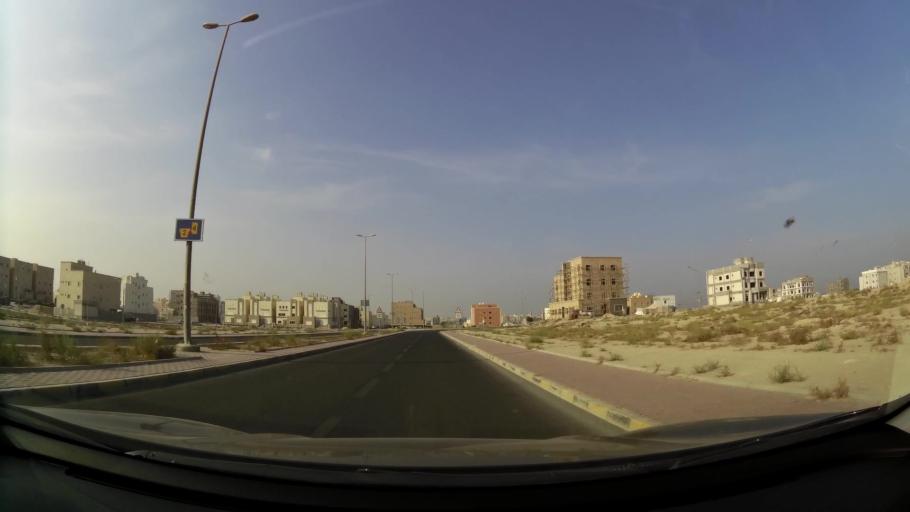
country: KW
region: Mubarak al Kabir
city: Mubarak al Kabir
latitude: 29.2015
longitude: 48.1011
